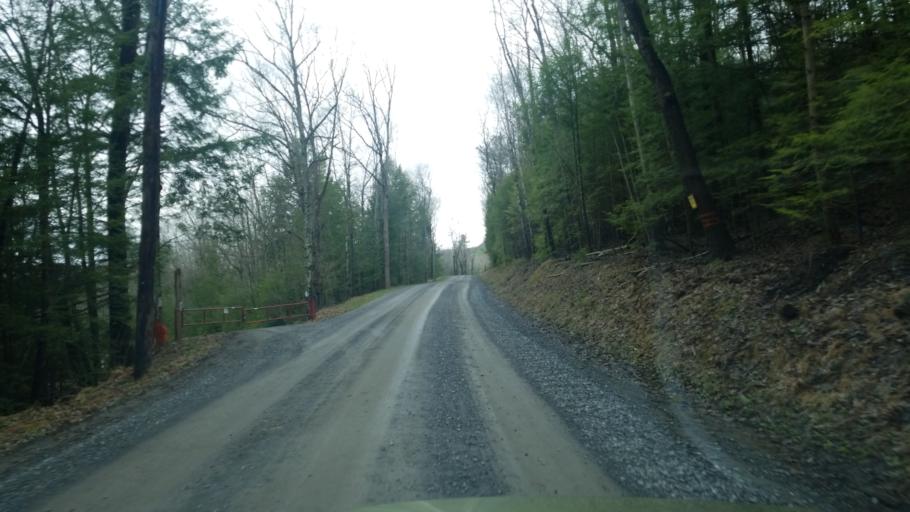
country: US
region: Pennsylvania
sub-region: Clearfield County
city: Shiloh
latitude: 41.1186
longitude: -78.3413
